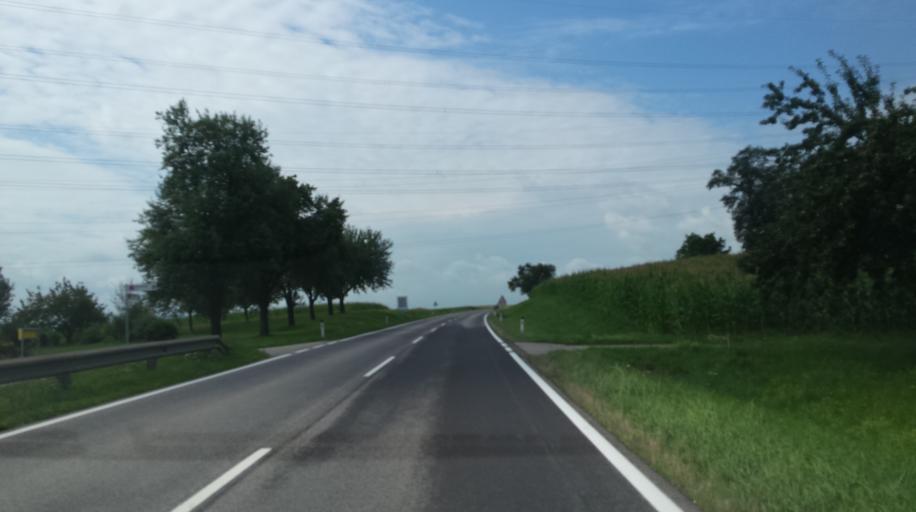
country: AT
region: Lower Austria
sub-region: Politischer Bezirk Amstetten
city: Haag
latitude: 48.1221
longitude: 14.5944
